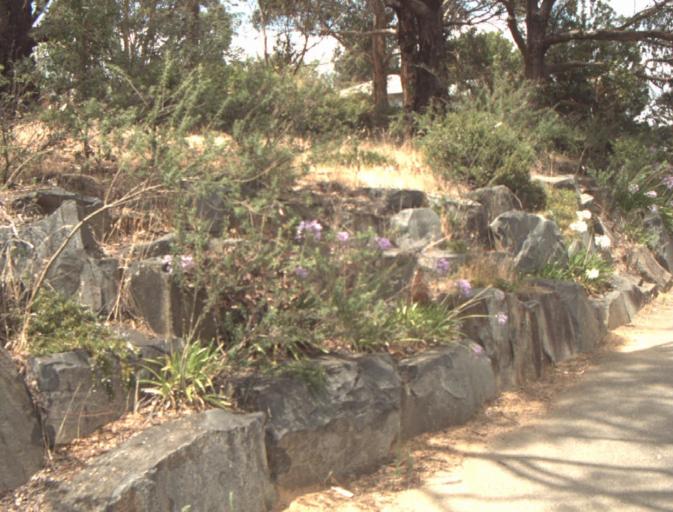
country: AU
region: Tasmania
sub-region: Launceston
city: East Launceston
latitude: -41.4558
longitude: 147.1508
